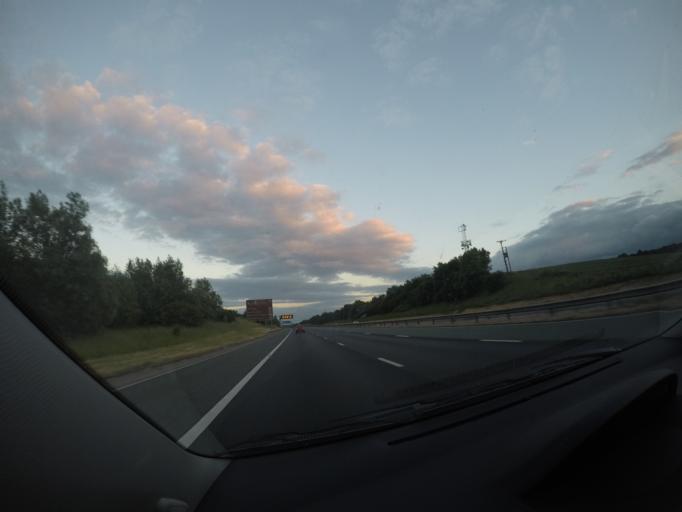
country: GB
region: England
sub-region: North Yorkshire
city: Boroughbridge
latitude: 54.0262
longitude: -1.3839
